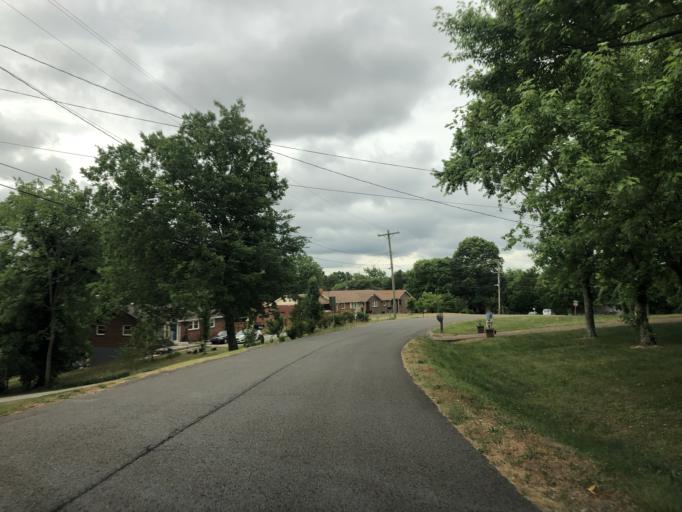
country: US
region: Tennessee
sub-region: Davidson County
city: Goodlettsville
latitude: 36.2630
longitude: -86.7691
